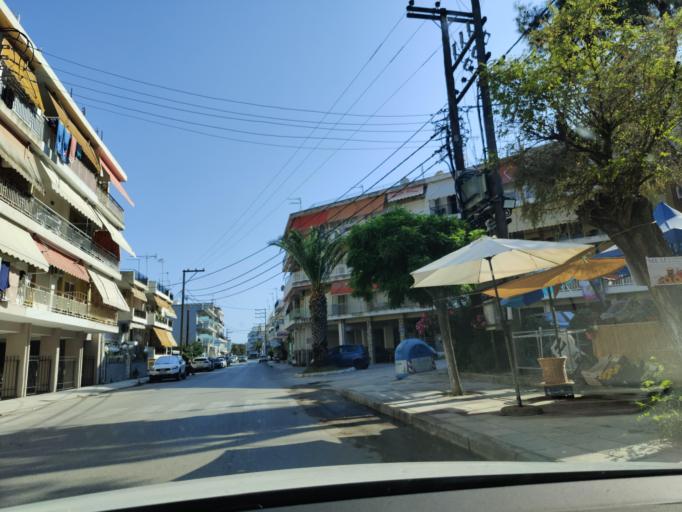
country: GR
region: East Macedonia and Thrace
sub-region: Nomos Kavalas
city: Nea Peramos
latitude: 40.8440
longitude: 24.3061
